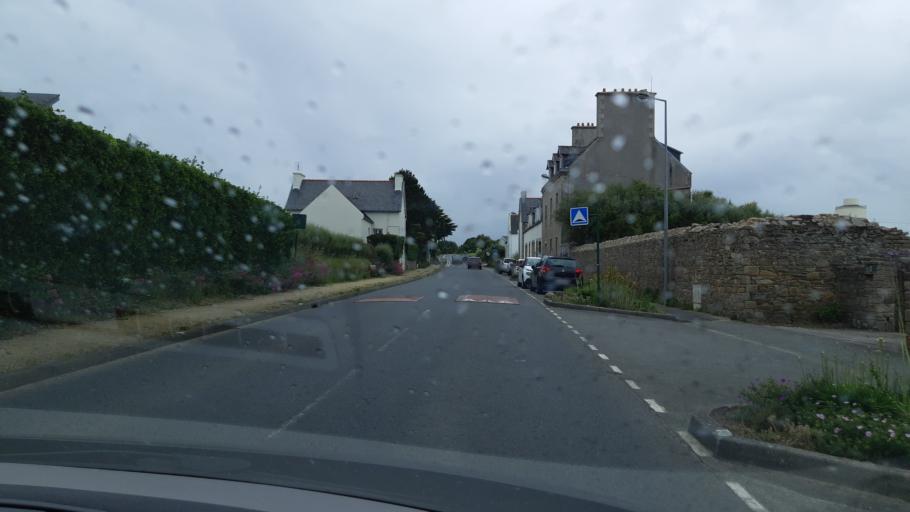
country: FR
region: Brittany
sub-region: Departement du Finistere
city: Roscoff
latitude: 48.7159
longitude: -3.9844
